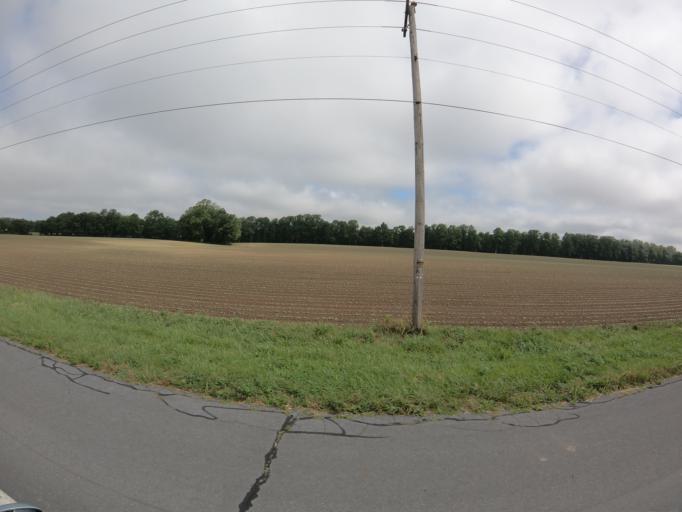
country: US
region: Delaware
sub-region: Kent County
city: Riverview
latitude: 39.0055
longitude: -75.5343
